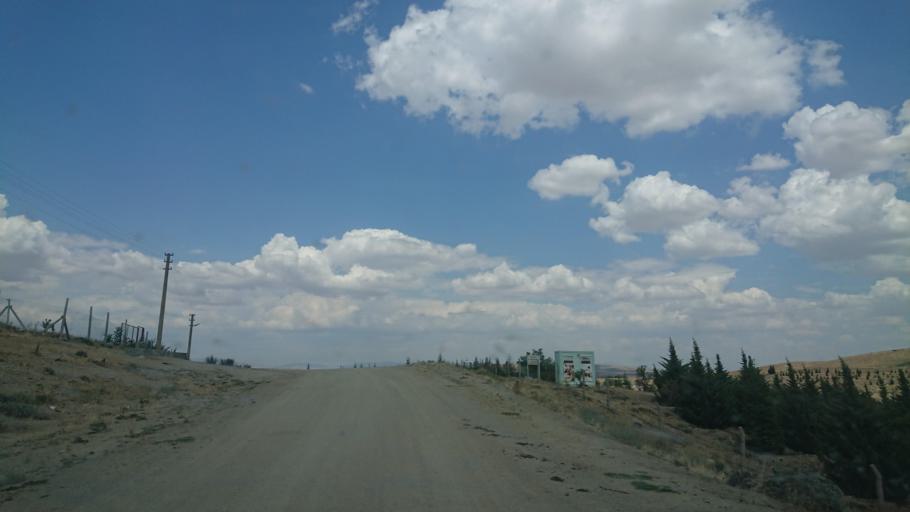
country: TR
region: Aksaray
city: Sariyahsi
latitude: 38.9500
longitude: 33.8814
